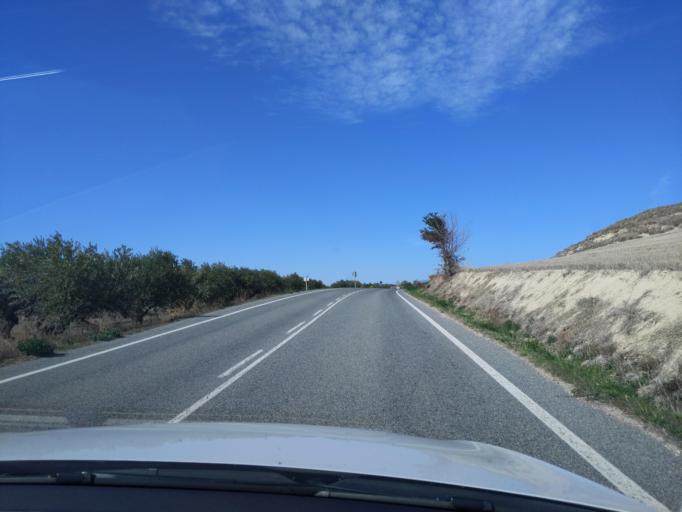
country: ES
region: Navarre
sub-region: Provincia de Navarra
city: Arroniz
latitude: 42.5679
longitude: -2.0716
